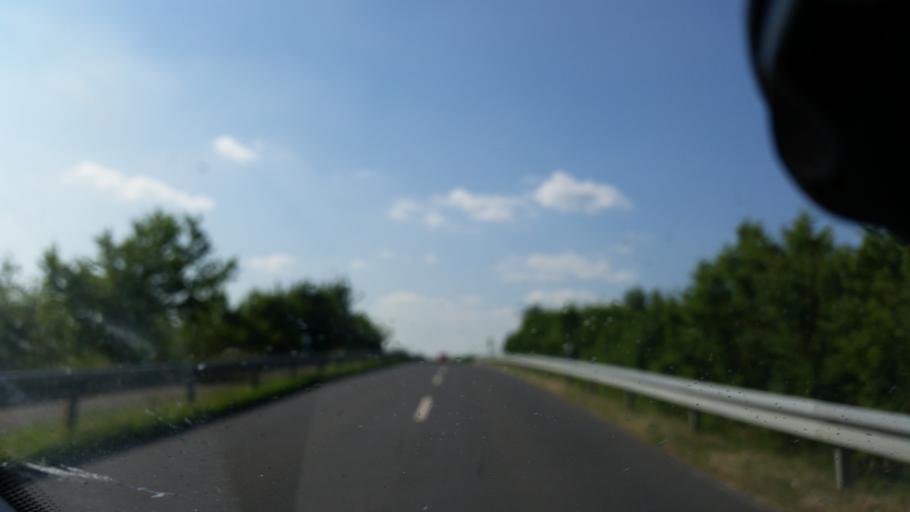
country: DE
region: Lower Saxony
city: Konigslutter am Elm
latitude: 52.3111
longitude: 10.7615
